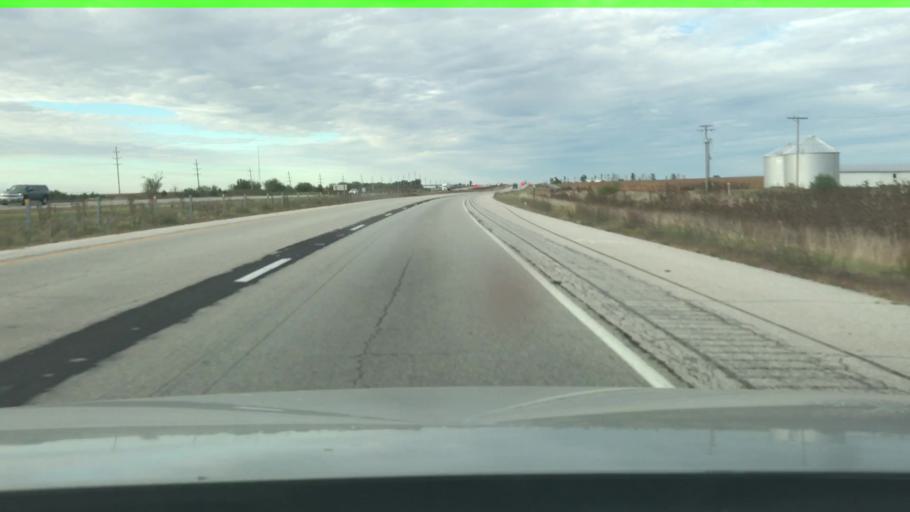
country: US
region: Illinois
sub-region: Livingston County
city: Odell
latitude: 40.9845
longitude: -88.5440
